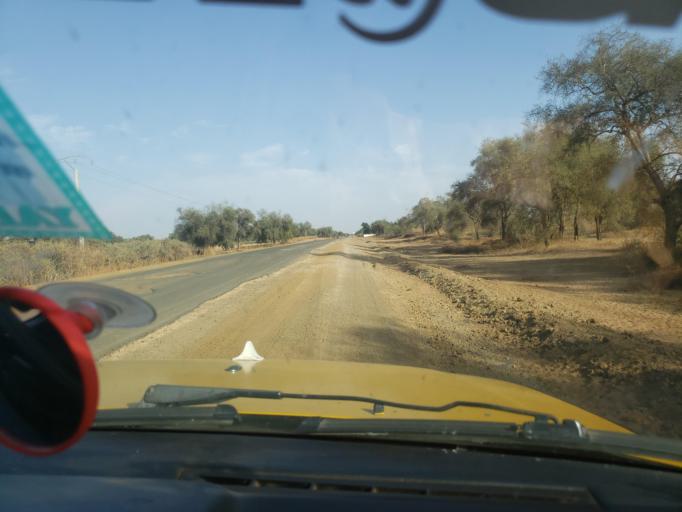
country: SN
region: Louga
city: Louga
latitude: 15.5033
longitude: -15.9497
